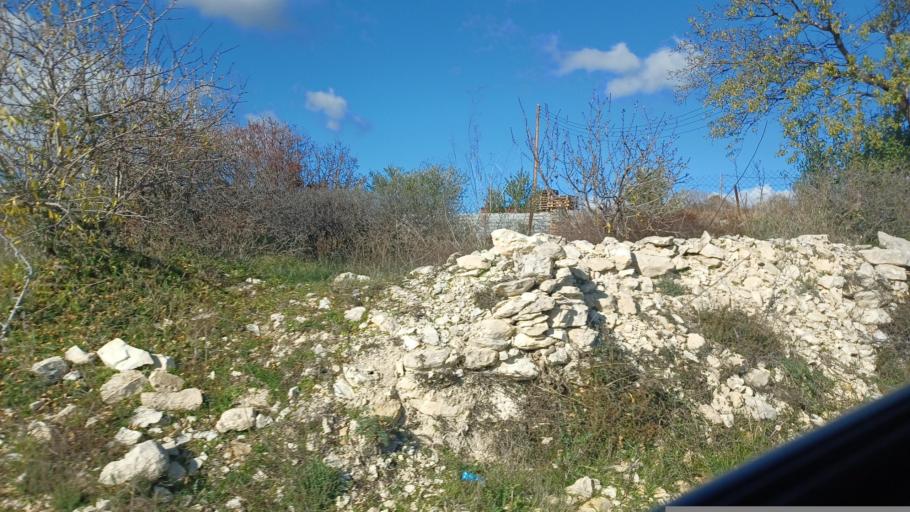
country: CY
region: Limassol
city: Pachna
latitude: 34.8331
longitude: 32.7985
